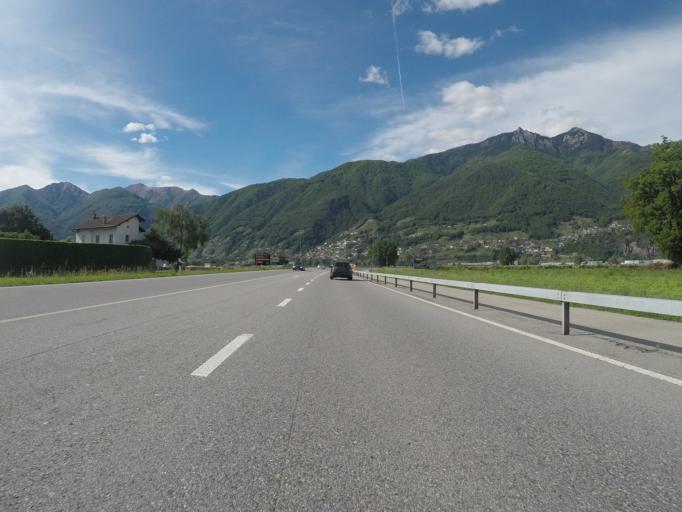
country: CH
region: Ticino
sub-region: Locarno District
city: Gordola
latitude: 46.1635
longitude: 8.8863
